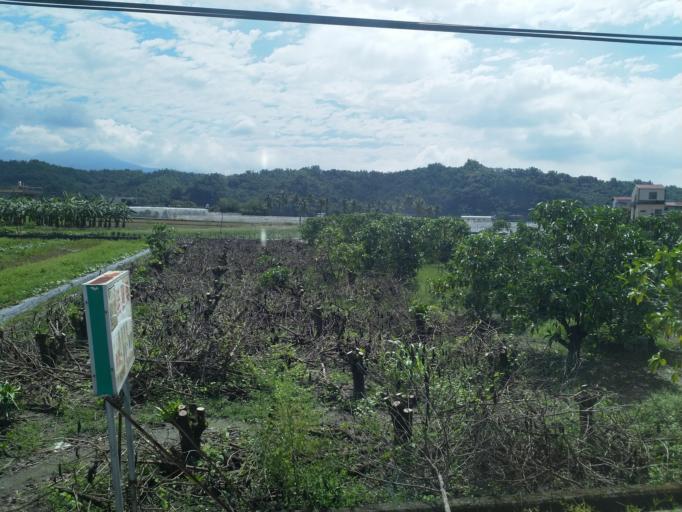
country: TW
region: Taiwan
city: Yujing
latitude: 22.9085
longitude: 120.5599
